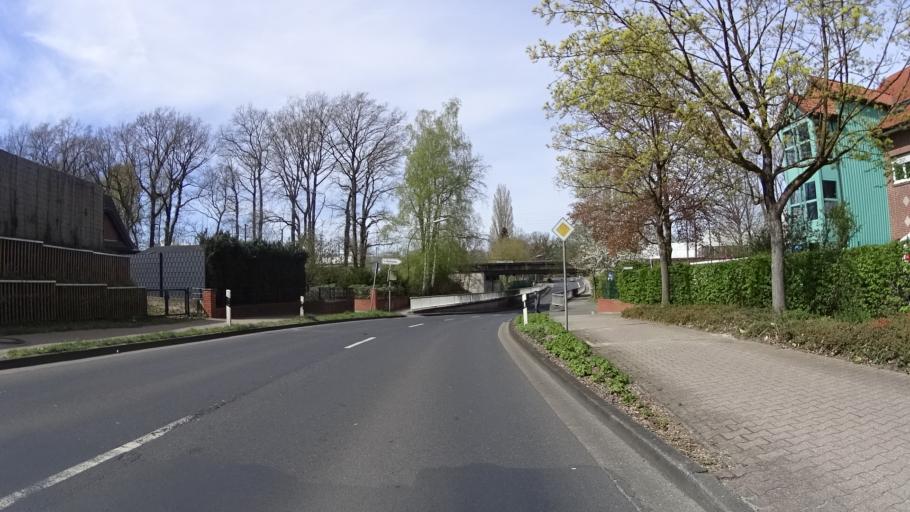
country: DE
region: Lower Saxony
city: Lingen
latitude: 52.5021
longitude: 7.3102
